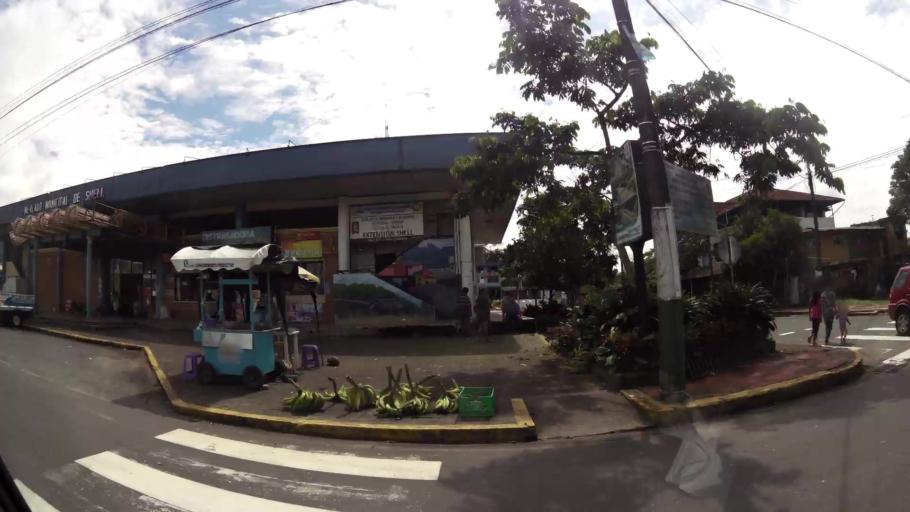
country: EC
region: Pastaza
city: Puyo
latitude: -1.5002
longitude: -78.0611
